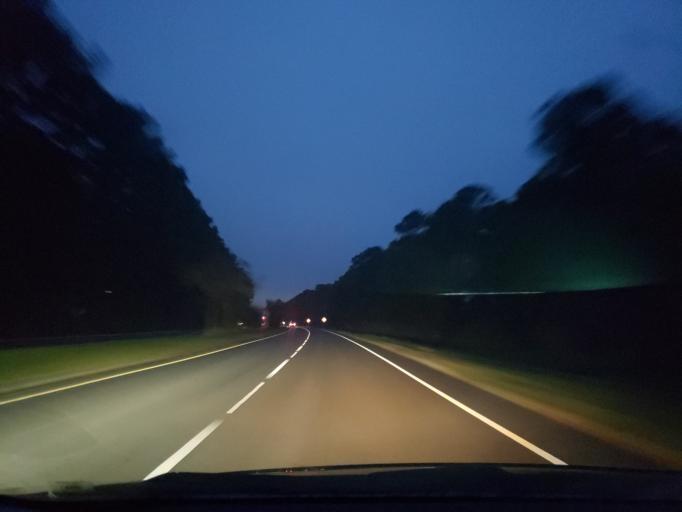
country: US
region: Georgia
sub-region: Chatham County
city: Whitemarsh Island
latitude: 32.0426
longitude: -81.0179
